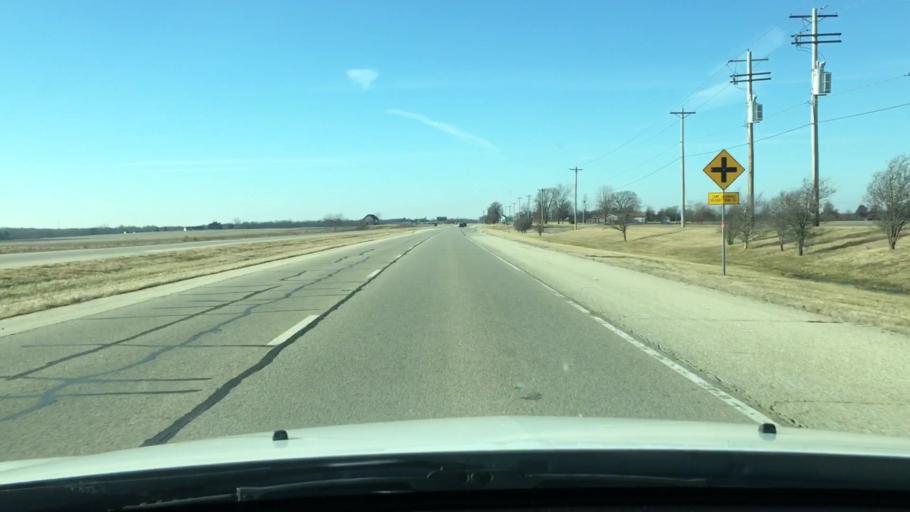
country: US
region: Illinois
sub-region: Woodford County
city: Metamora
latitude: 40.7781
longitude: -89.4141
